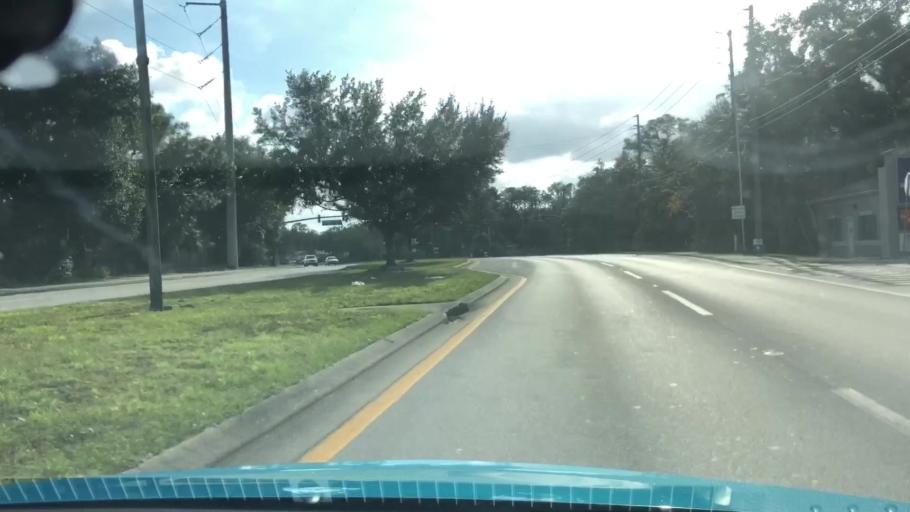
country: US
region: Florida
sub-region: Seminole County
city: Longwood
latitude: 28.7145
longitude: -81.3418
